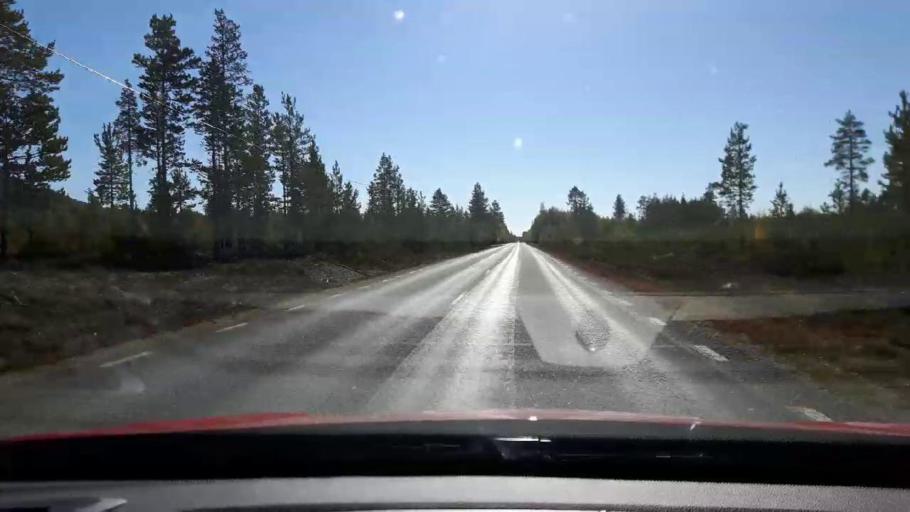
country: SE
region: Jaemtland
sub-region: Harjedalens Kommun
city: Sveg
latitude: 62.4086
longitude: 13.9231
